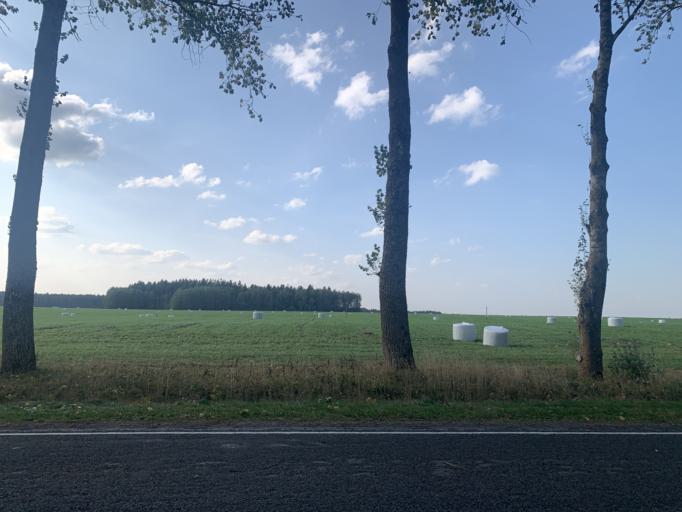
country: BY
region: Minsk
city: Ivyanyets
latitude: 53.8083
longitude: 26.6747
